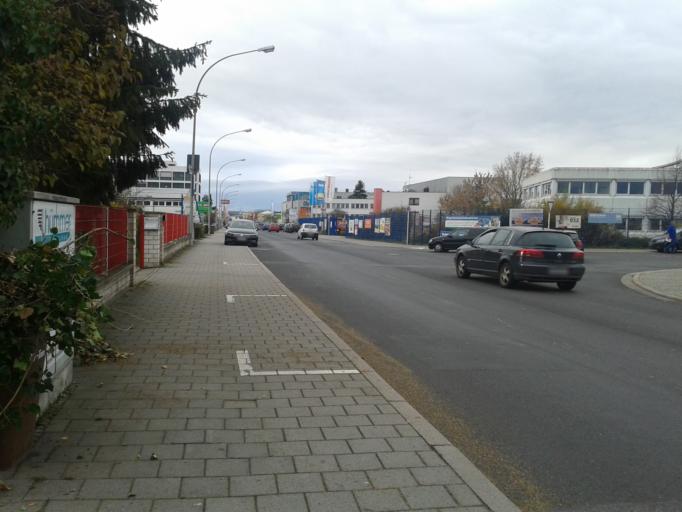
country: DE
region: Bavaria
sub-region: Upper Franconia
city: Hallstadt
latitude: 49.9110
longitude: 10.8733
